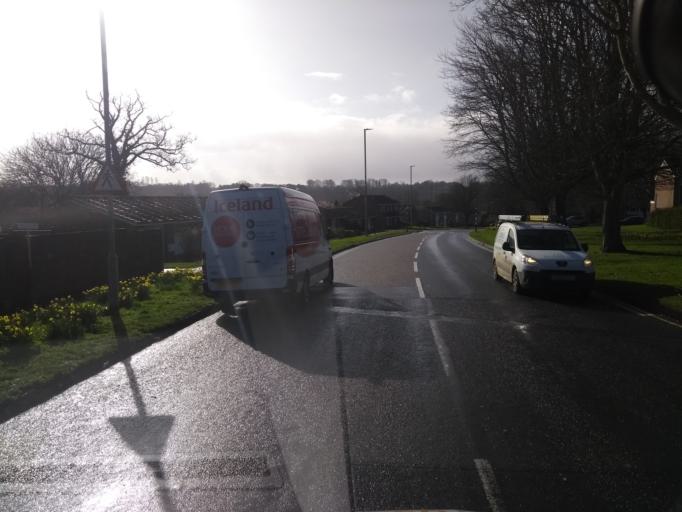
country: GB
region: England
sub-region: Somerset
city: Yeovil
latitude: 50.9524
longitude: -2.6087
